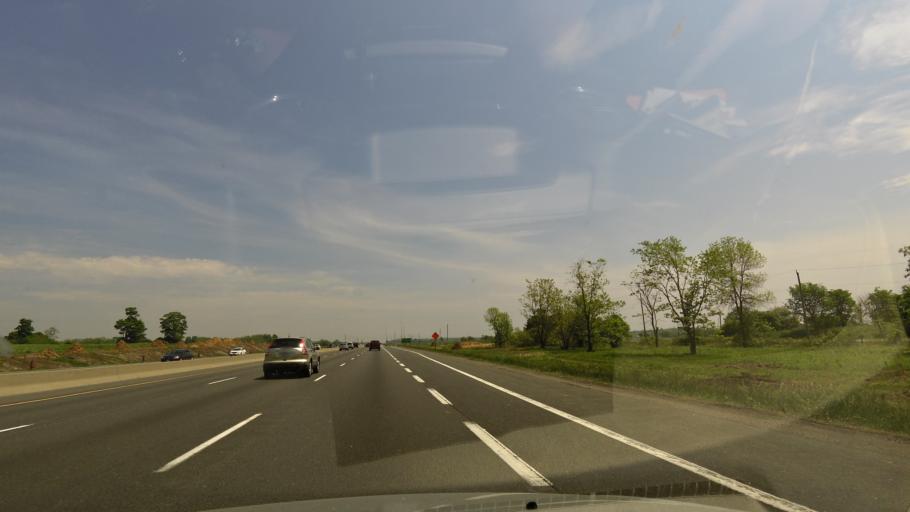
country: CA
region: Ontario
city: Oshawa
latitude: 43.8777
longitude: -78.7712
